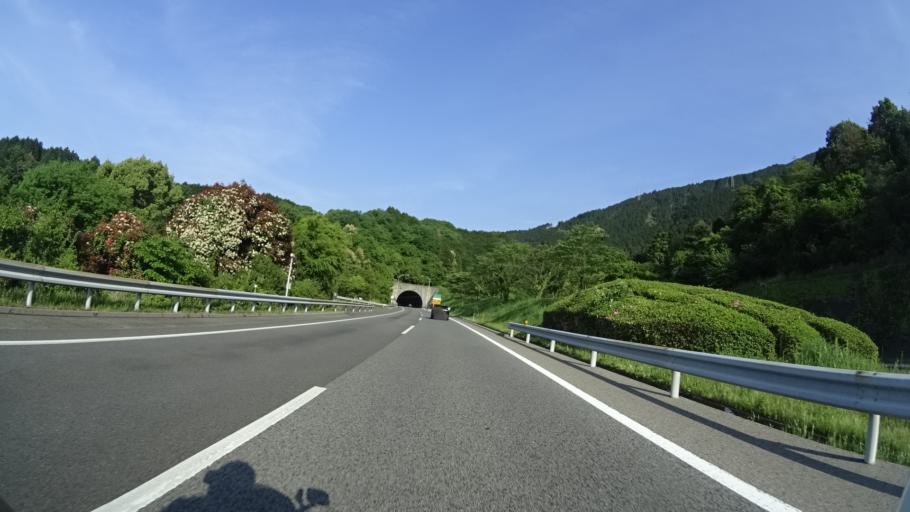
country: JP
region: Ehime
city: Saijo
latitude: 33.9095
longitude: 133.2506
